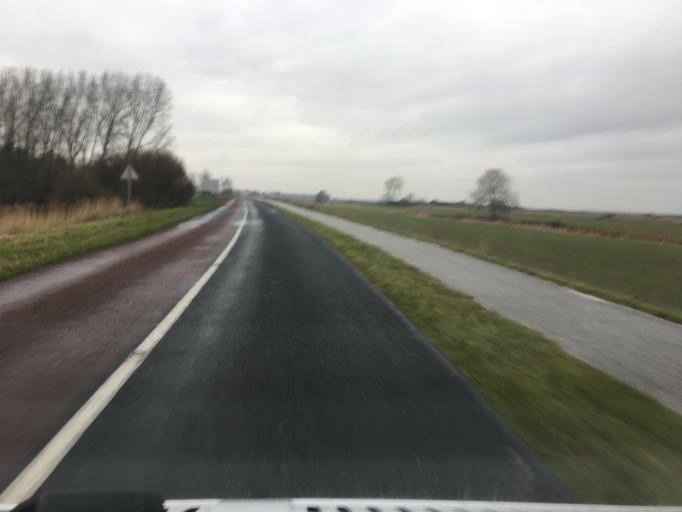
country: FR
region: Picardie
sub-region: Departement de la Somme
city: Pende
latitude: 50.2006
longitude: 1.5551
